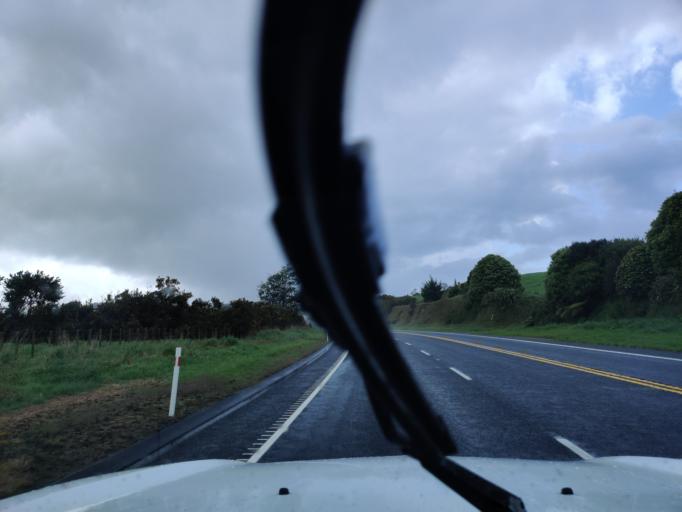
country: NZ
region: Waikato
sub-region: Matamata-Piako District
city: Matamata
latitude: -37.9933
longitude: 175.8530
